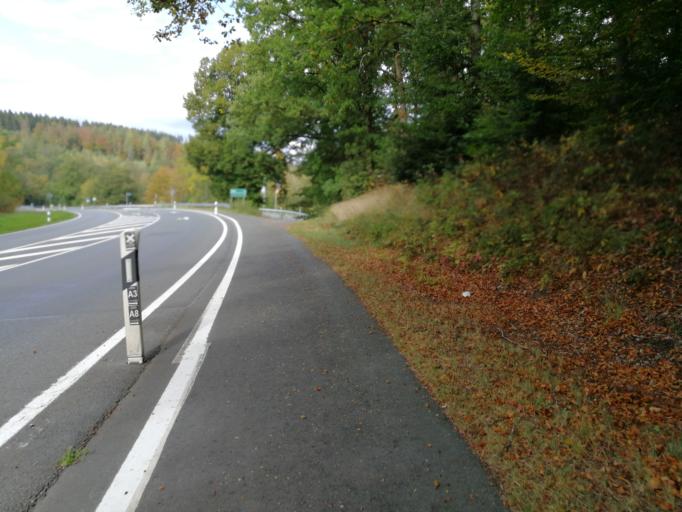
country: DE
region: North Rhine-Westphalia
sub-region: Regierungsbezirk Arnsberg
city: Meschede
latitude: 51.3297
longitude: 8.2565
